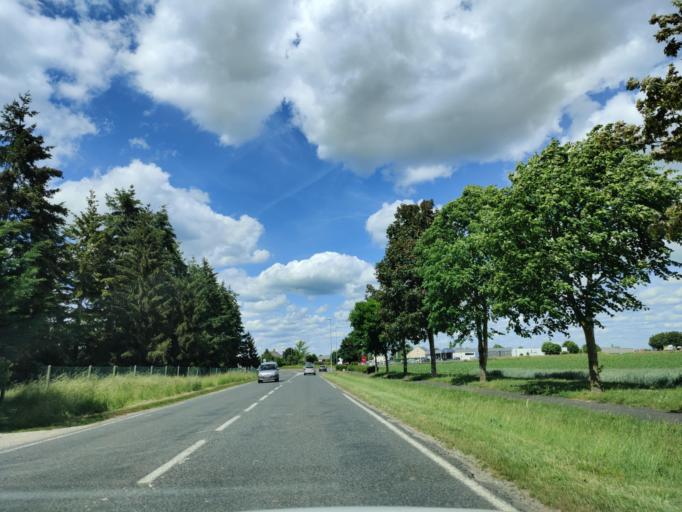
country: FR
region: Centre
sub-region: Departement du Loiret
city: Pithiviers
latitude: 48.1595
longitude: 2.2583
